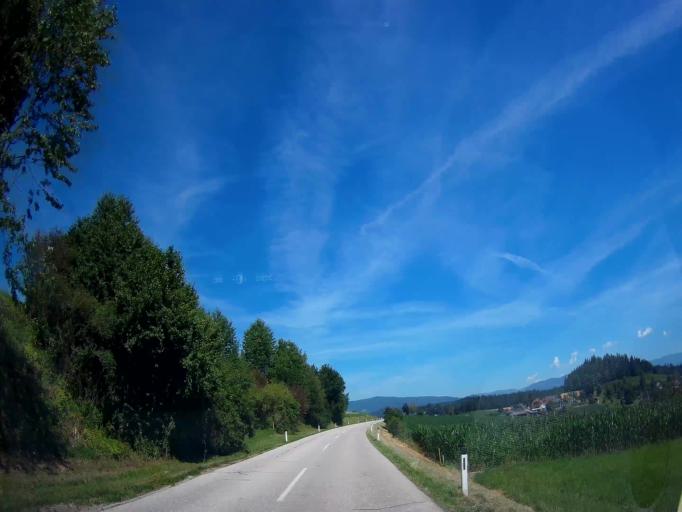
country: AT
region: Carinthia
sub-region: Politischer Bezirk Sankt Veit an der Glan
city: St. Georgen am Laengsee
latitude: 46.7913
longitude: 14.4185
